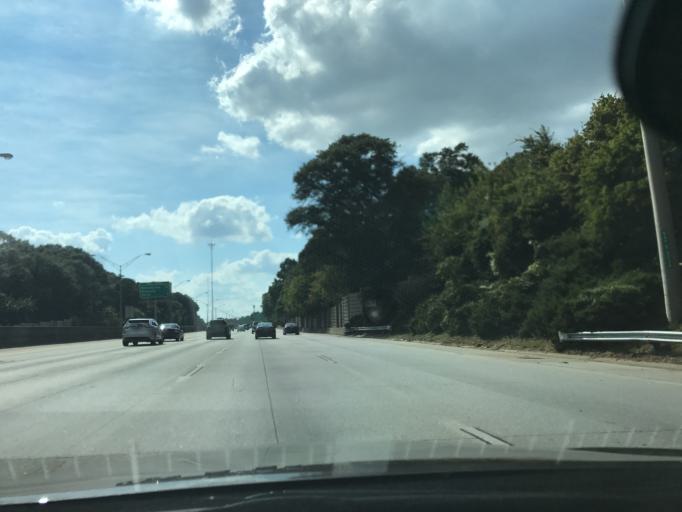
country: US
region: Georgia
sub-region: DeKalb County
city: Druid Hills
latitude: 33.7457
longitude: -84.3403
